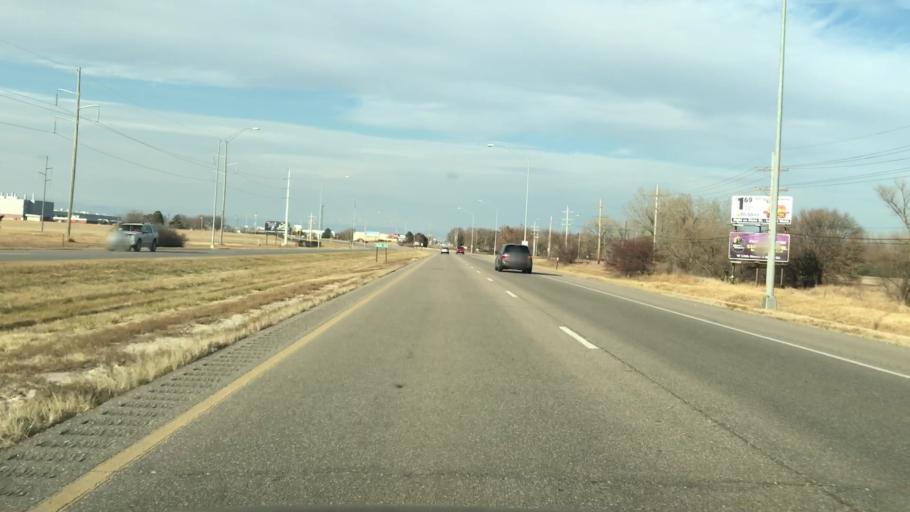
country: US
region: Nebraska
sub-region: Hall County
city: Grand Island
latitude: 40.8930
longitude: -98.3783
